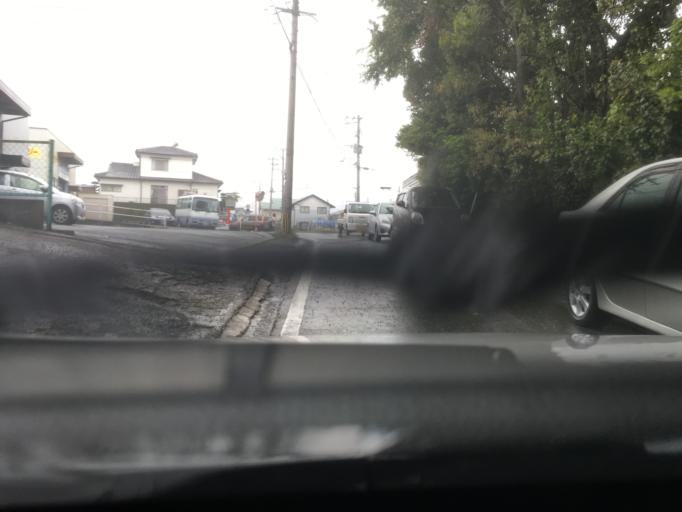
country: JP
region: Kumamoto
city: Ueki
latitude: 32.8715
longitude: 130.7021
